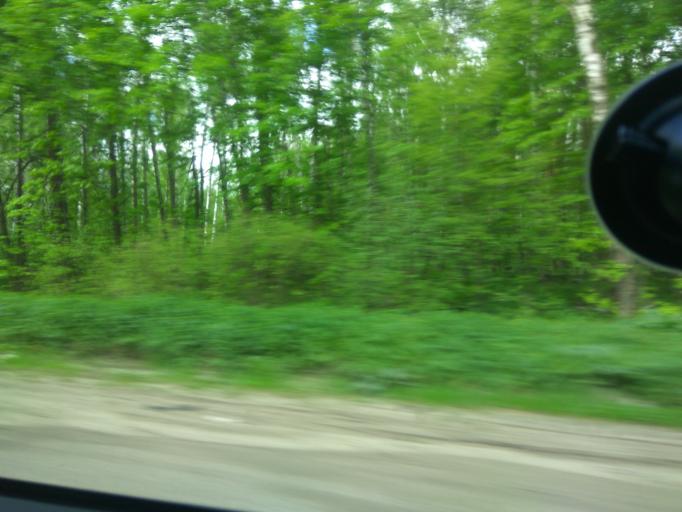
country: RU
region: Moskovskaya
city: Andreyevskoye
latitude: 55.5353
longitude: 37.8964
